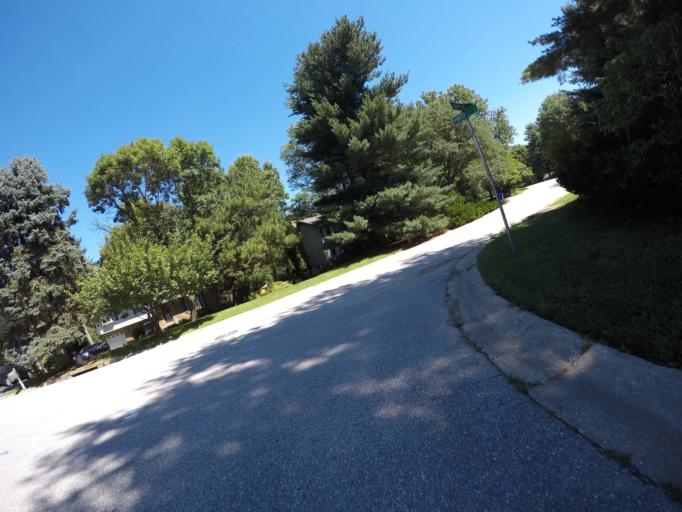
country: US
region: Maryland
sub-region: Howard County
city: Columbia
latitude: 39.2429
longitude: -76.8172
